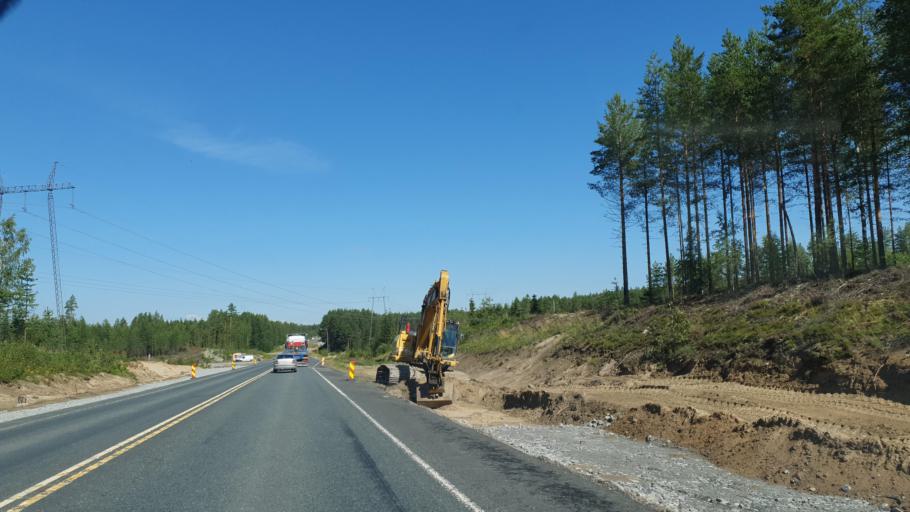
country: FI
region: Northern Savo
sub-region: Ylae-Savo
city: Lapinlahti
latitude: 63.2705
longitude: 27.4629
